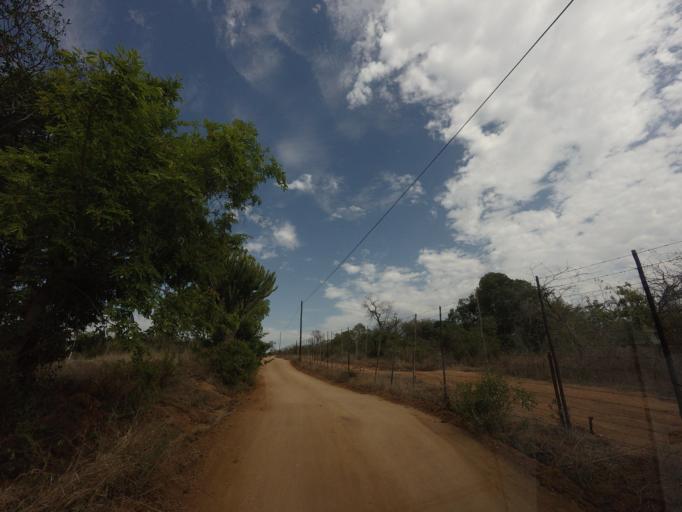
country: ZA
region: Limpopo
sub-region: Mopani District Municipality
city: Hoedspruit
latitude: -24.5108
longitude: 31.1056
